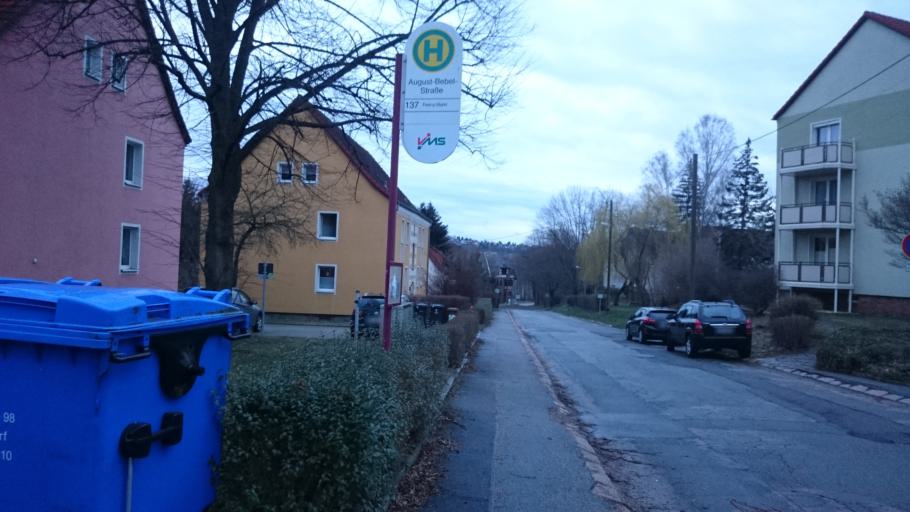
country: DE
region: Saxony
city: Wilkau-Hasslau
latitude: 50.6799
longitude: 12.5081
